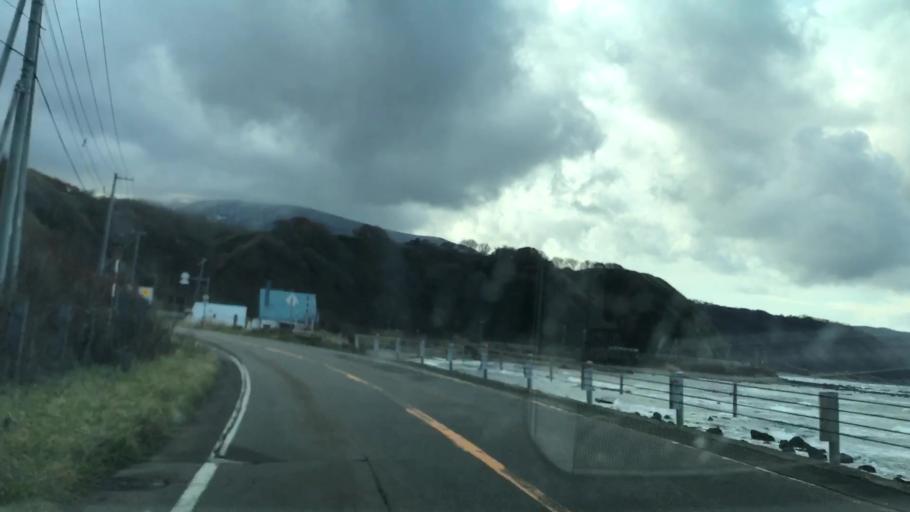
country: JP
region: Hokkaido
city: Yoichi
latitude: 43.3411
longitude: 140.4538
